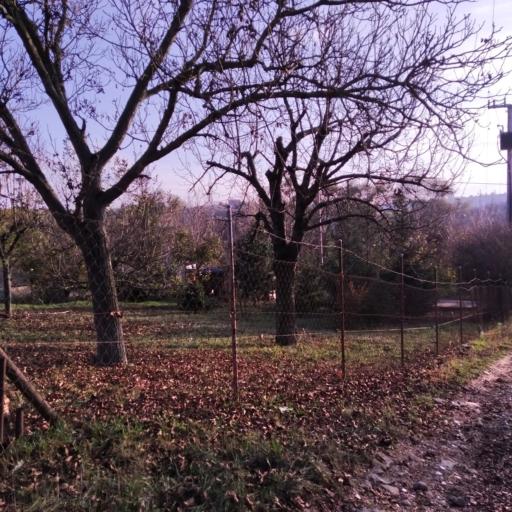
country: HU
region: Pest
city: Pomaz
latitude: 47.6258
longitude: 19.0318
